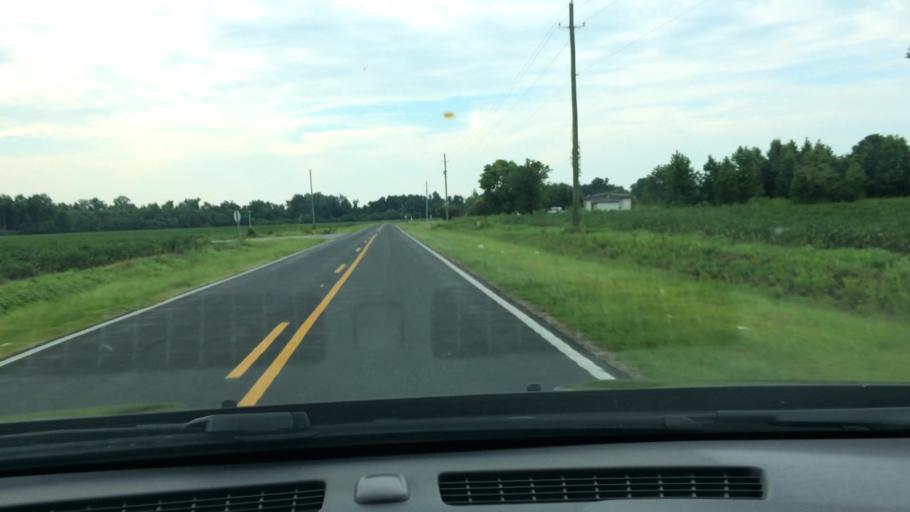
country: US
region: North Carolina
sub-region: Pitt County
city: Ayden
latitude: 35.4422
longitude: -77.4101
